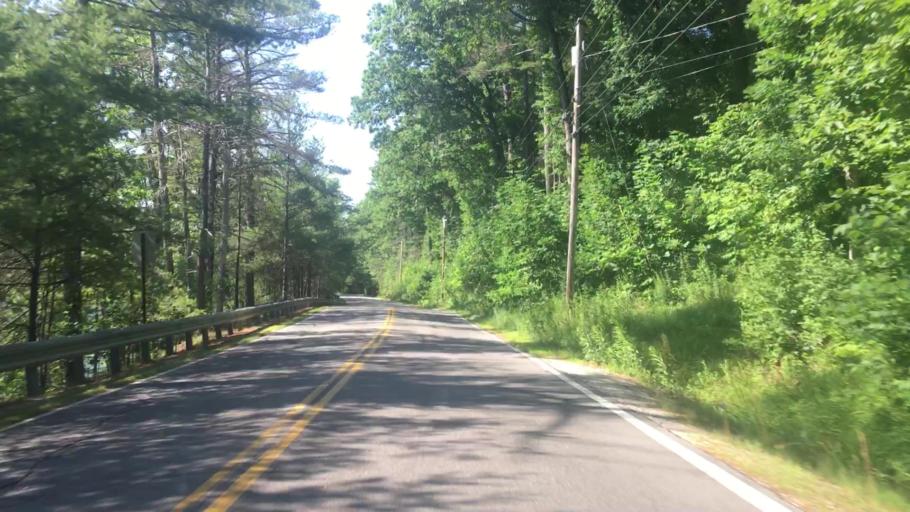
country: US
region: Maine
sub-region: York County
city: Hollis Center
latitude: 43.6610
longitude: -70.5976
